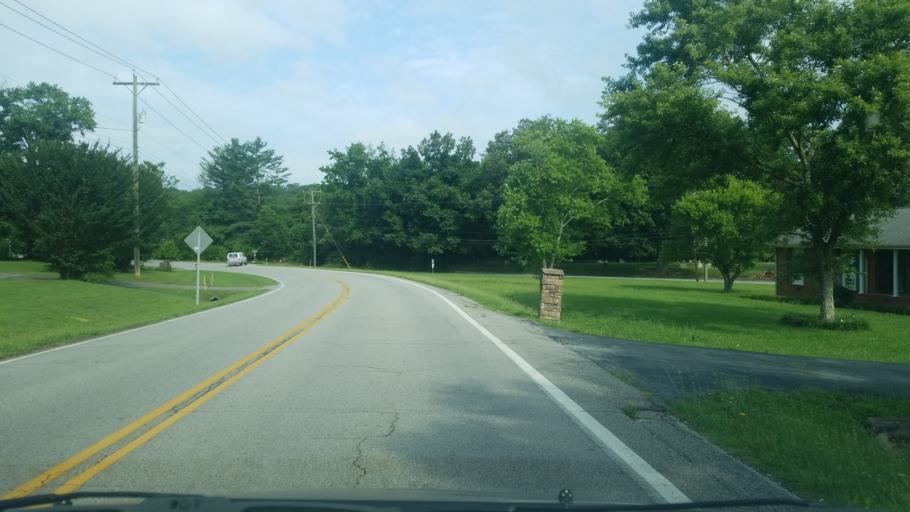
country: US
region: Tennessee
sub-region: Hamilton County
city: Apison
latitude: 35.0169
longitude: -85.0308
